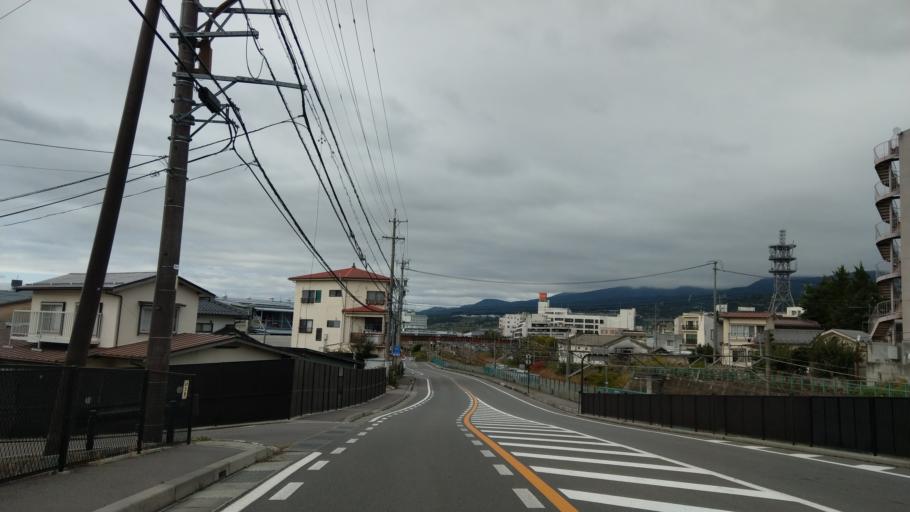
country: JP
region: Nagano
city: Komoro
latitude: 36.3229
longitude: 138.4257
